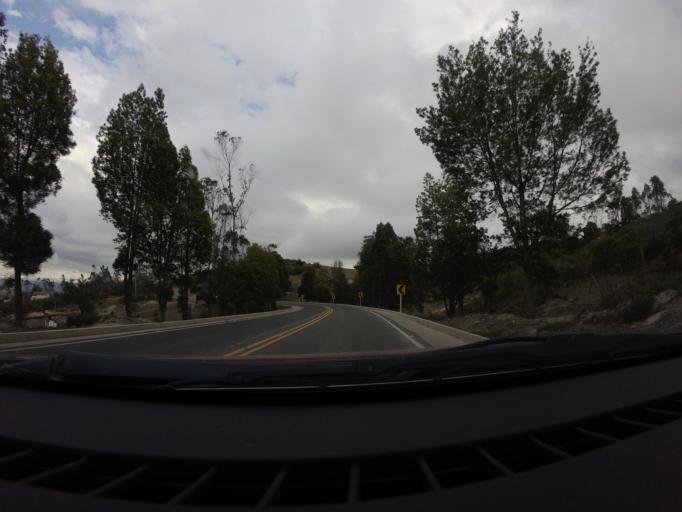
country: CO
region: Boyaca
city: Cucaita
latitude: 5.5602
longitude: -73.4108
